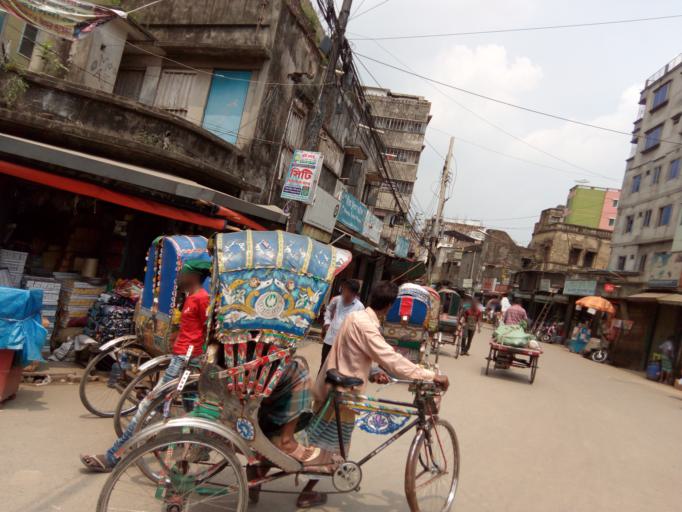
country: BD
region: Dhaka
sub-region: Dhaka
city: Dhaka
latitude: 23.7155
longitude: 90.4114
